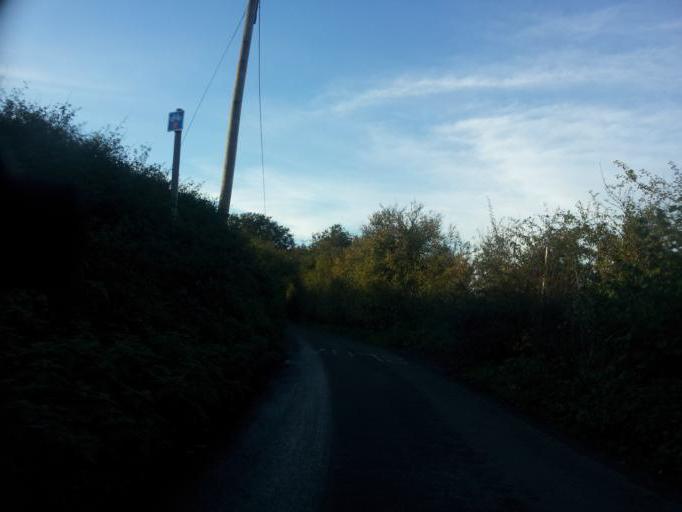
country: GB
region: England
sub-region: Kent
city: Newington
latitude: 51.3585
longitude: 0.6689
